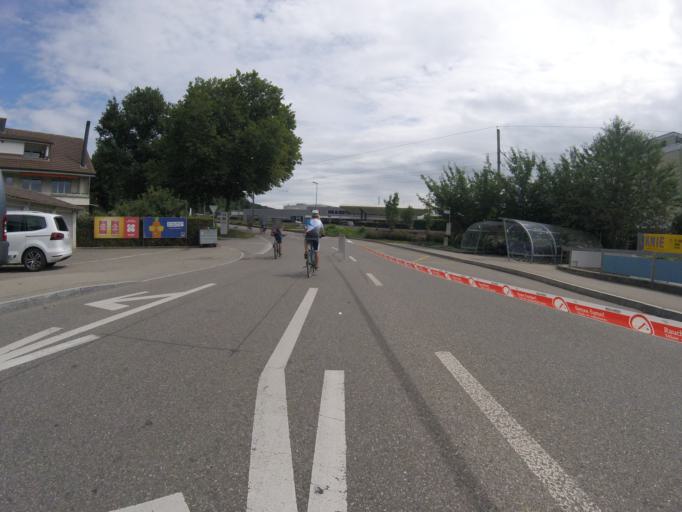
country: CH
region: Bern
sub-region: Bern-Mittelland District
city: Muri
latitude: 46.9356
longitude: 7.4986
